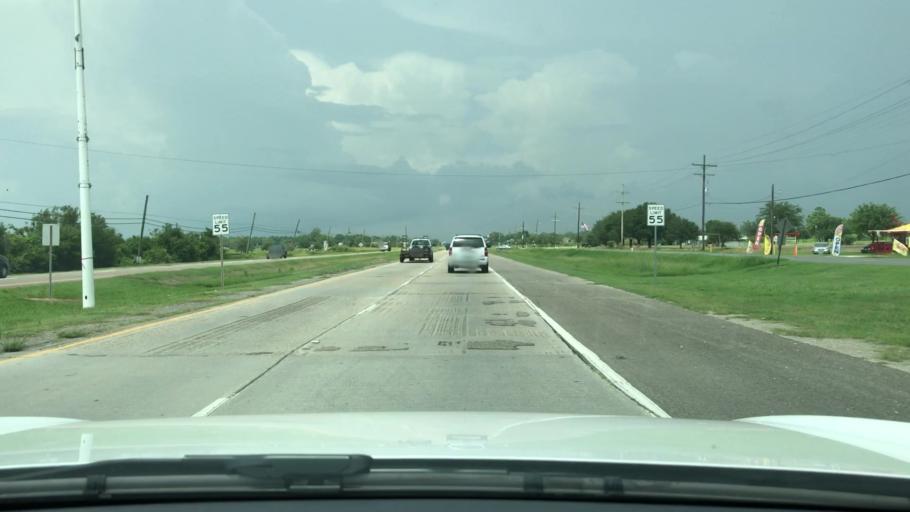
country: US
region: Louisiana
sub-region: West Baton Rouge Parish
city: Brusly
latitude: 30.3951
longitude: -91.2386
